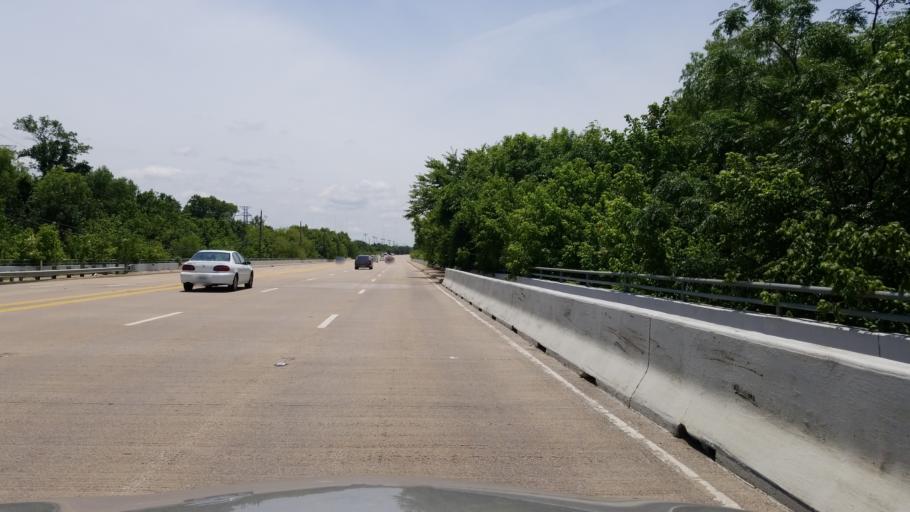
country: US
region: Texas
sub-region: Dallas County
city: Grand Prairie
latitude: 32.6917
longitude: -96.9854
